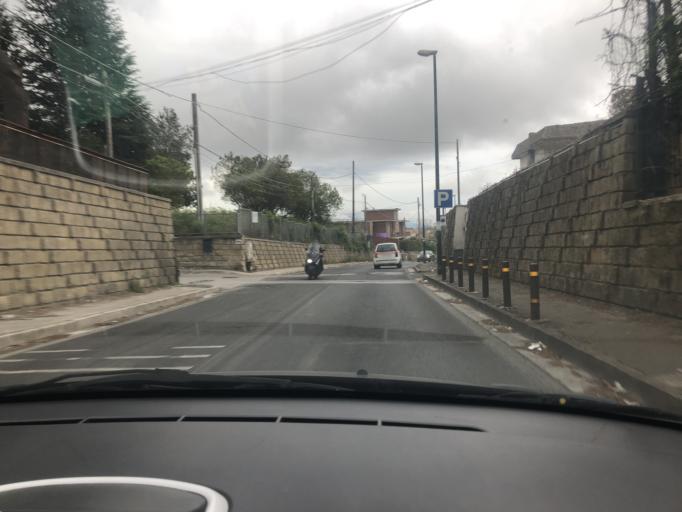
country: IT
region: Campania
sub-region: Provincia di Napoli
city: Torre Caracciolo
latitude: 40.8640
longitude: 14.1979
